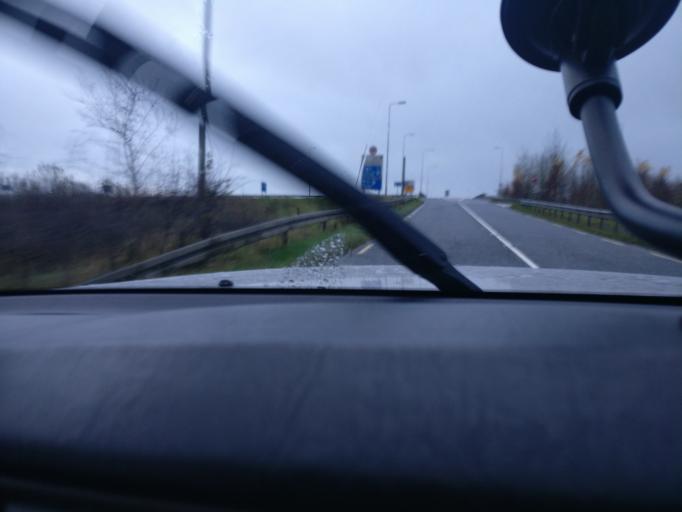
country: IE
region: Leinster
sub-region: An Iarmhi
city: Kinnegad
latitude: 53.4506
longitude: -7.1231
